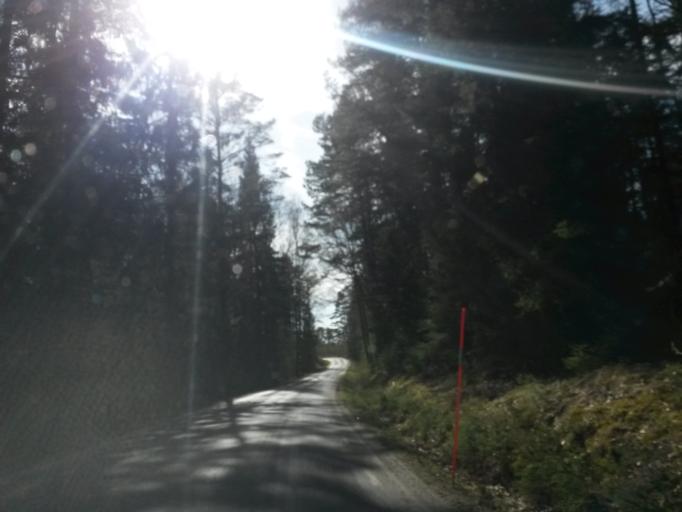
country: SE
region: Vaestra Goetaland
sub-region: Vargarda Kommun
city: Jonstorp
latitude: 57.9447
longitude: 12.7066
